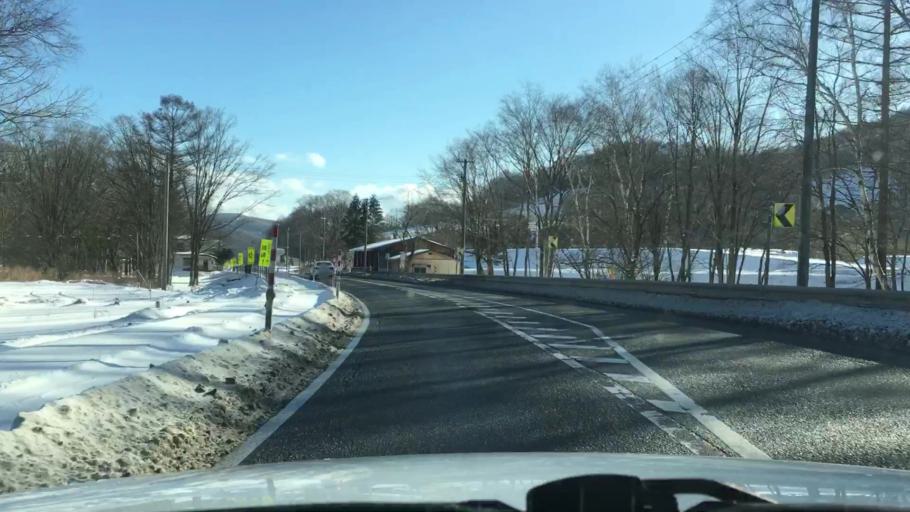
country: JP
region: Iwate
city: Morioka-shi
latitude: 39.6427
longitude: 141.3782
